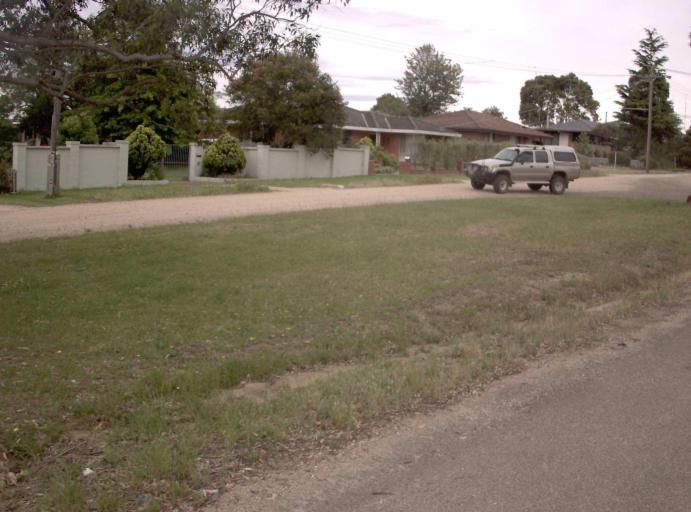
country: AU
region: Victoria
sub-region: East Gippsland
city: Bairnsdale
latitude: -37.8036
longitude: 147.6159
